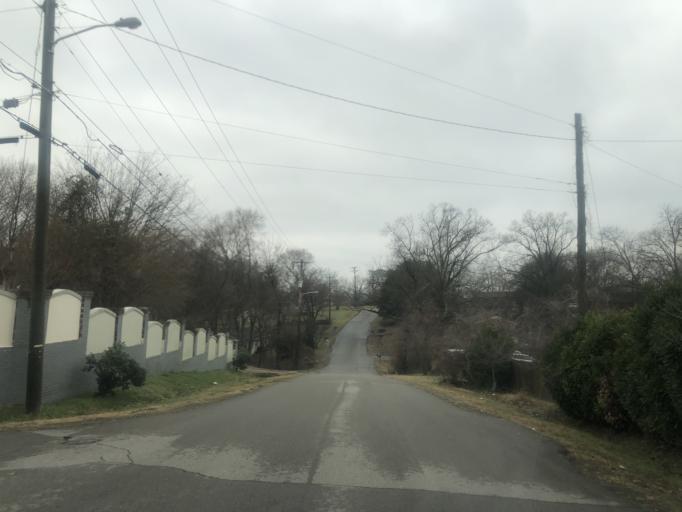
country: US
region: Tennessee
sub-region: Davidson County
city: Lakewood
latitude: 36.1450
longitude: -86.6696
